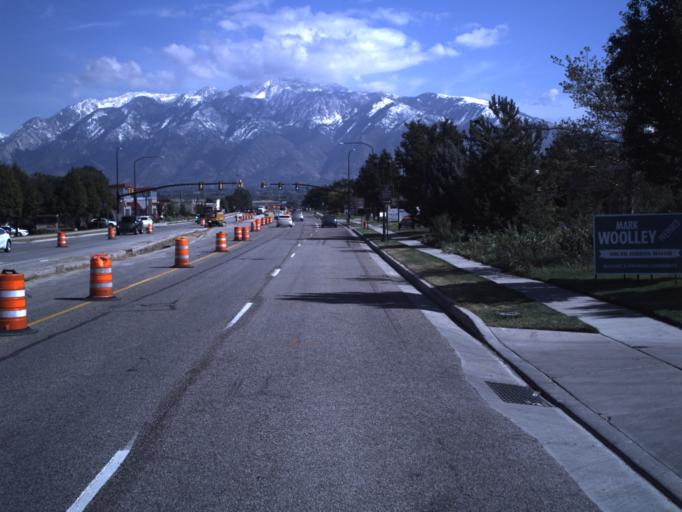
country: US
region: Utah
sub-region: Salt Lake County
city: South Jordan
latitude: 40.5608
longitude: -111.9223
